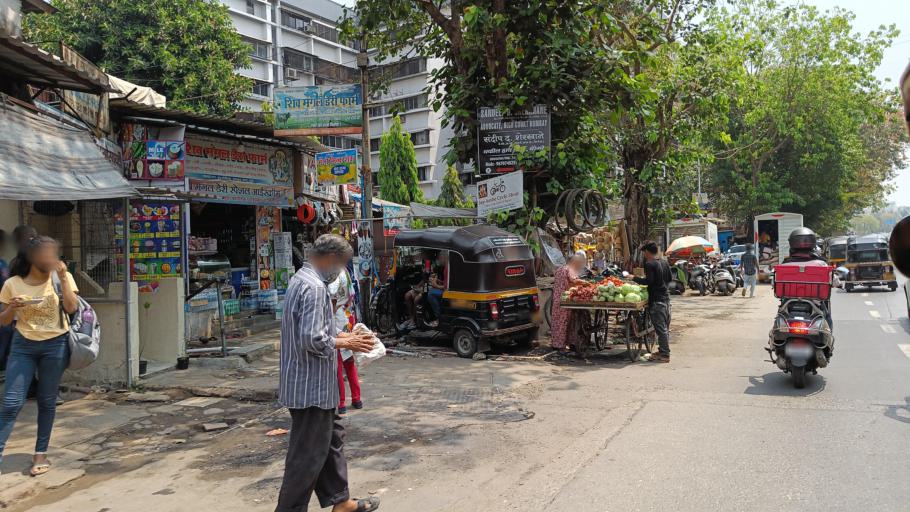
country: IN
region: Maharashtra
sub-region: Mumbai Suburban
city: Mumbai
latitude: 19.0860
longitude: 72.8282
